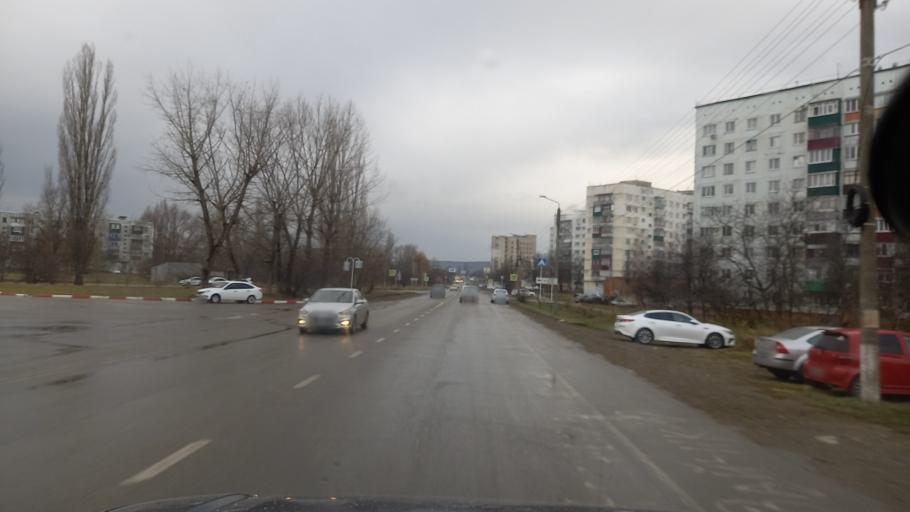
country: RU
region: Adygeya
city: Maykop
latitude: 44.5793
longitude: 40.1358
